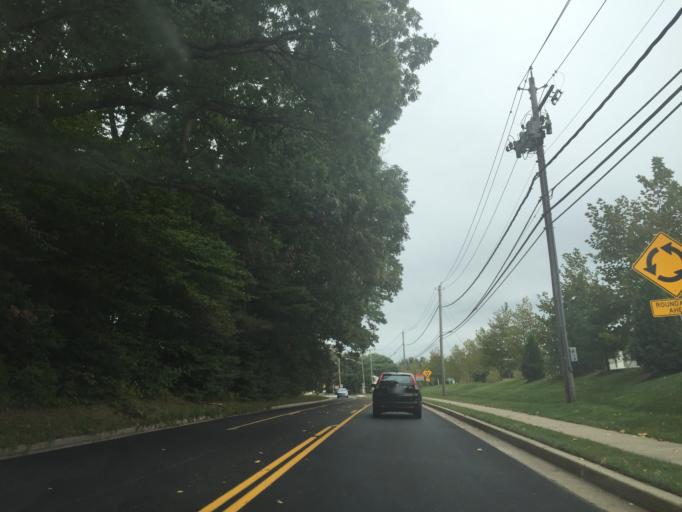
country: US
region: Maryland
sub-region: Harford County
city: South Bel Air
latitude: 39.5103
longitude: -76.3465
